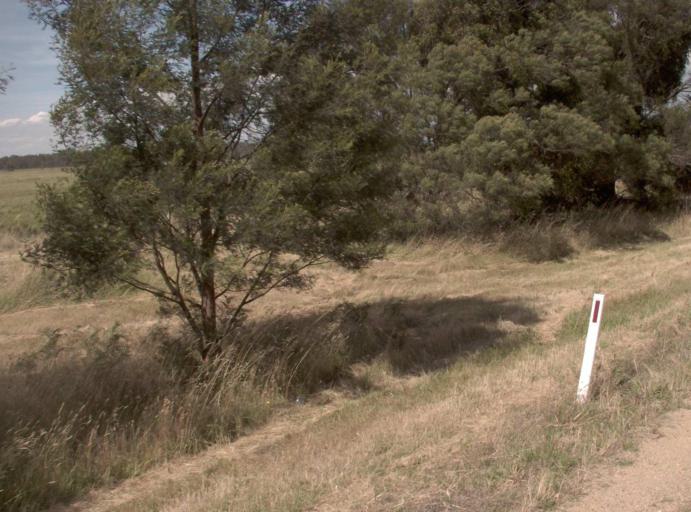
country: AU
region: Victoria
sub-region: Wellington
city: Sale
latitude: -38.1627
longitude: 146.9384
